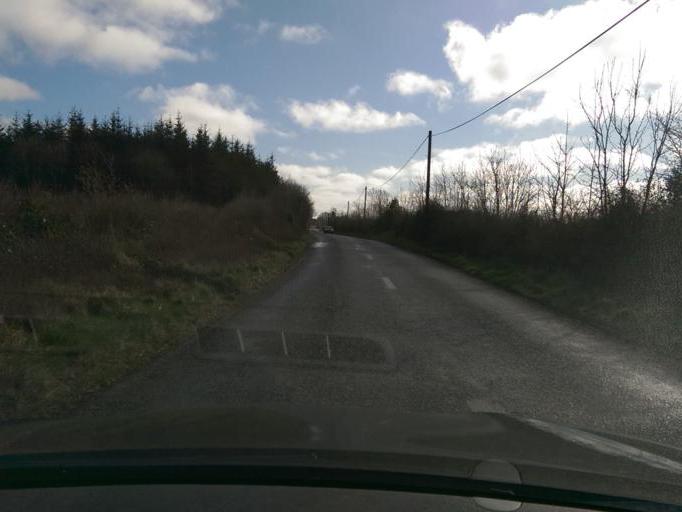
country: IE
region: Connaught
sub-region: County Galway
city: Ballinasloe
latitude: 53.4144
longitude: -8.3585
